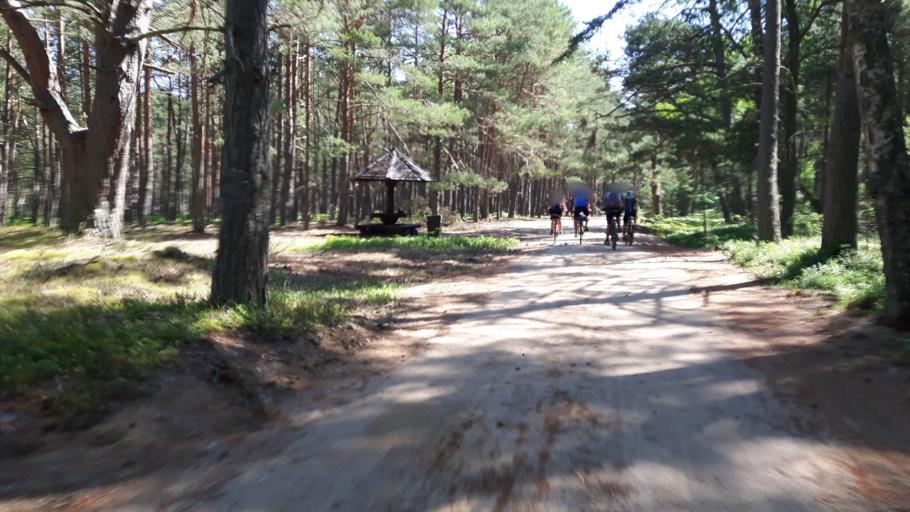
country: PL
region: Pomeranian Voivodeship
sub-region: Powiat slupski
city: Smoldzino
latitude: 54.6786
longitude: 17.1429
